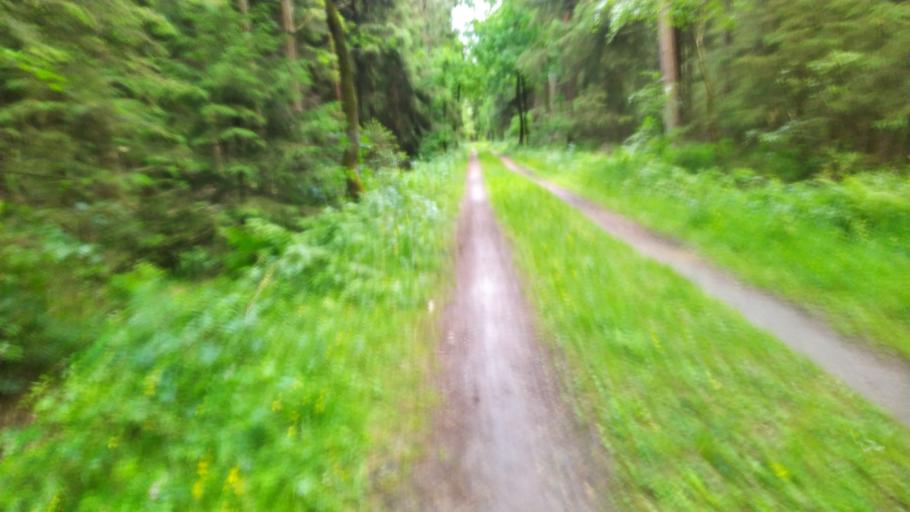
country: DE
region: Lower Saxony
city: Deinstedt
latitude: 53.4402
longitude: 9.2468
